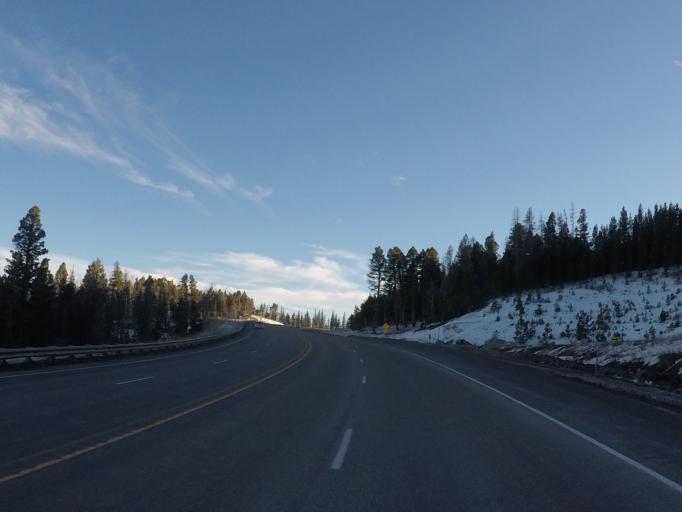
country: US
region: Montana
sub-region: Lewis and Clark County
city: Helena West Side
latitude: 46.5664
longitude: -112.3064
